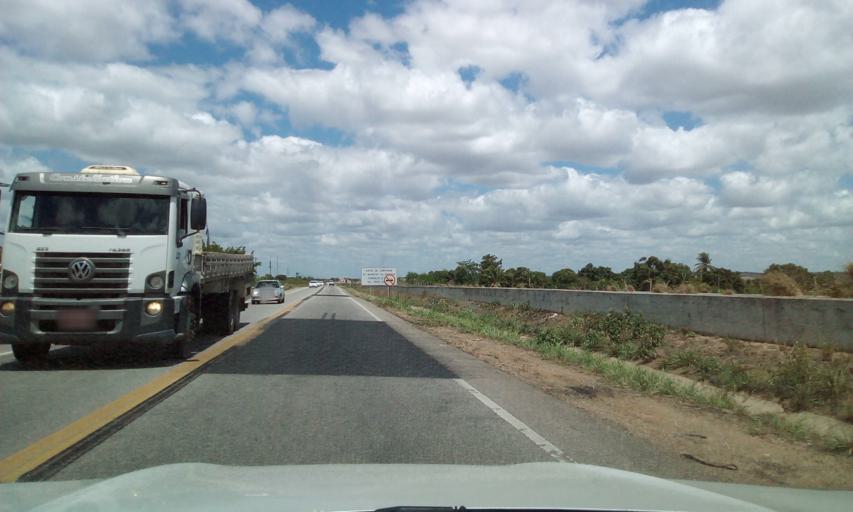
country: BR
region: Alagoas
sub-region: Porto Real Do Colegio
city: Porto Real do Colegio
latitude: -10.1981
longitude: -36.8214
